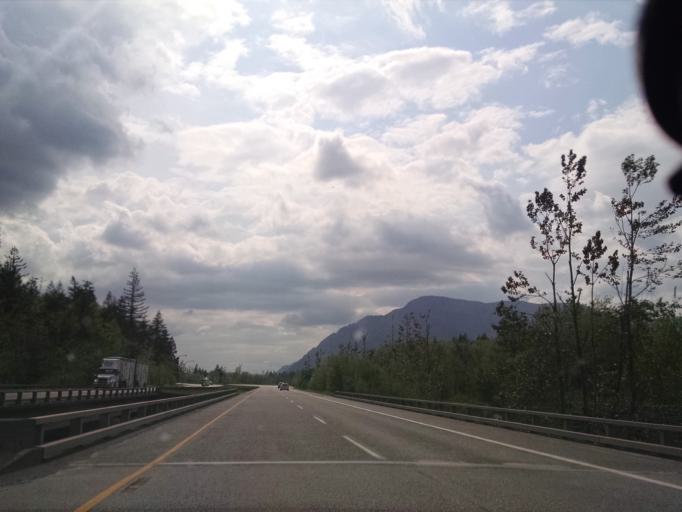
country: CA
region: British Columbia
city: Hope
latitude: 49.3583
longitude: -121.5734
